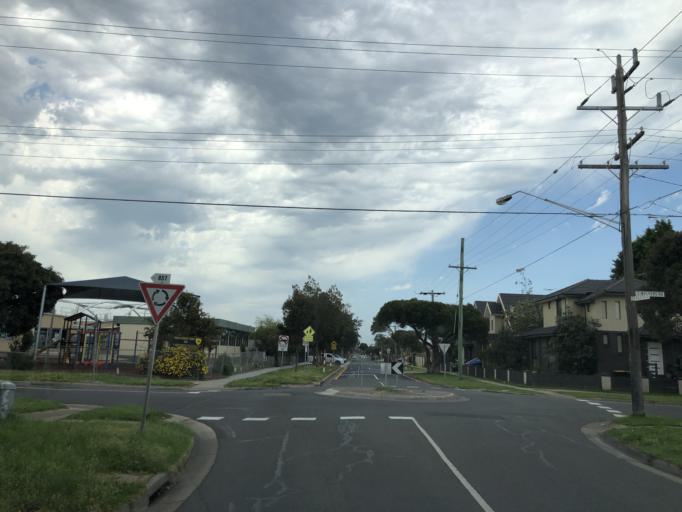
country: AU
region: Victoria
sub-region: Kingston
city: Carrum
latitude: -38.0778
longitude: 145.1256
